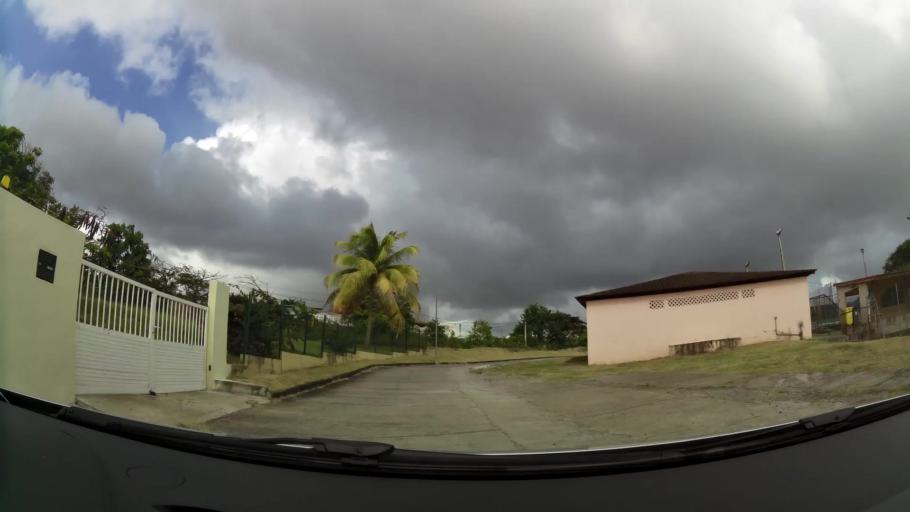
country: MQ
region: Martinique
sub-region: Martinique
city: Sainte-Luce
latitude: 14.4683
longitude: -60.9268
